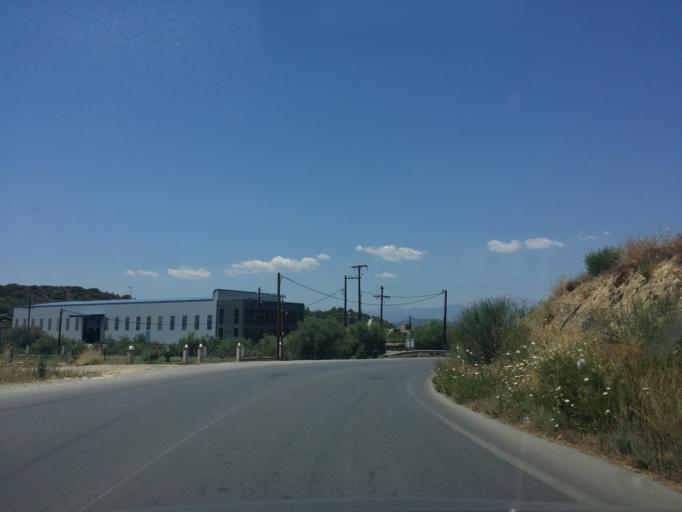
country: GR
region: Peloponnese
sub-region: Nomos Lakonias
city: Vlakhiotis
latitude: 36.8597
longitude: 22.7218
